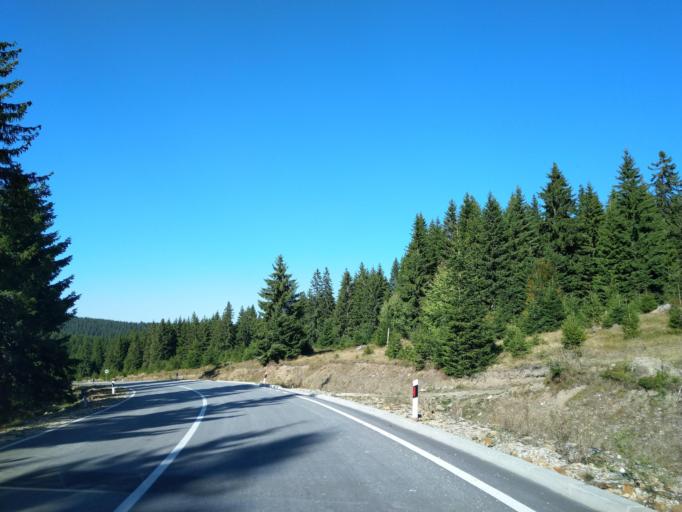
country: RS
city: Sokolovica
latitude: 43.3132
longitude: 20.2948
